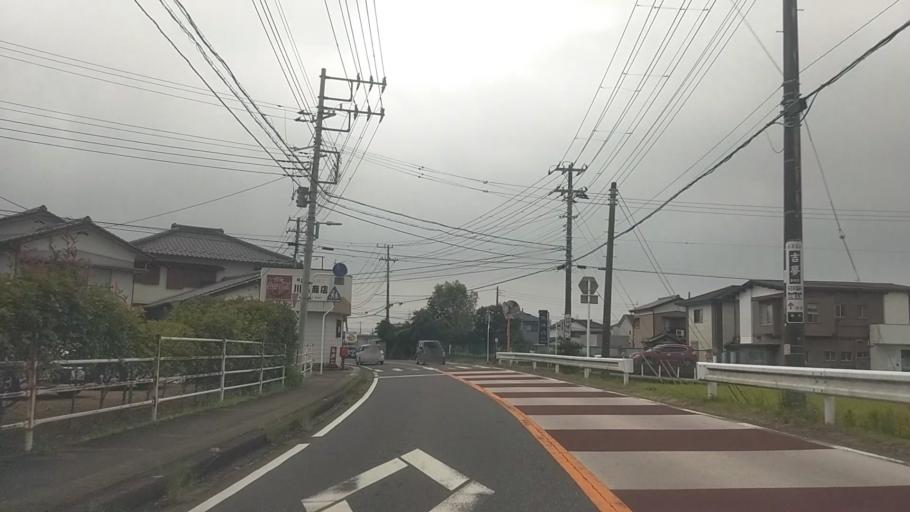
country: JP
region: Chiba
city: Kawaguchi
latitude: 35.1130
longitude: 140.0948
